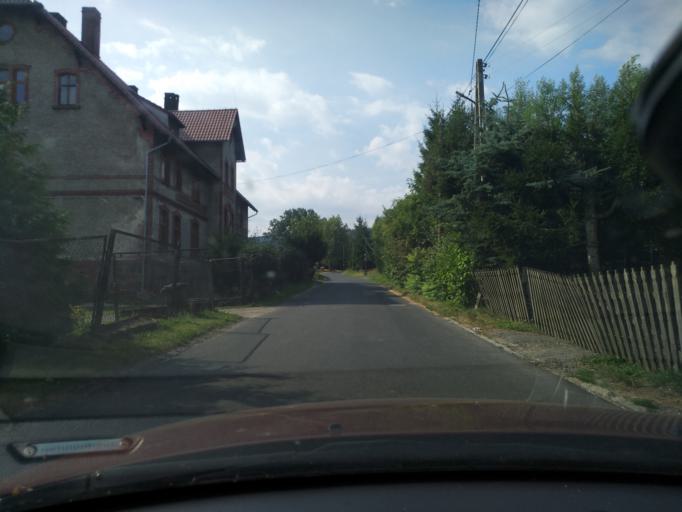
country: PL
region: Lower Silesian Voivodeship
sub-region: Powiat jeleniogorski
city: Stara Kamienica
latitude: 50.8910
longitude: 15.5515
